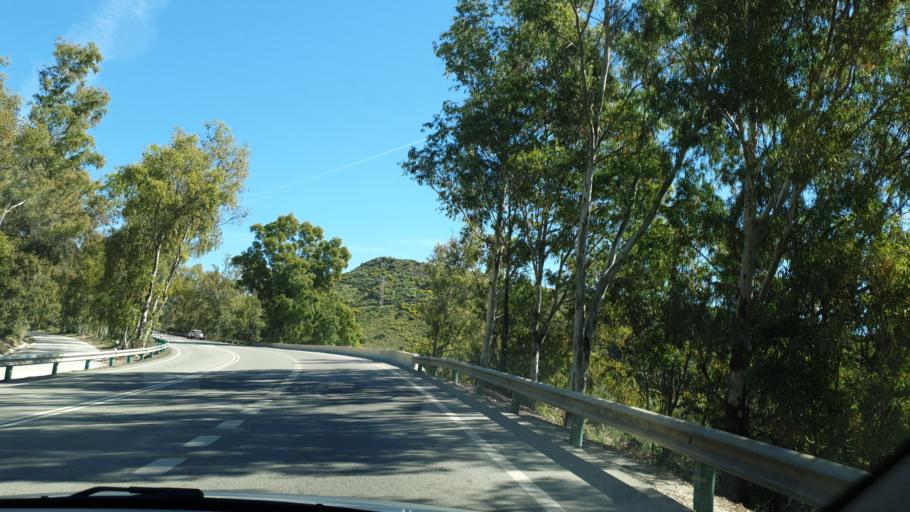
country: ES
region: Andalusia
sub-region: Provincia de Malaga
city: Marbella
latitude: 36.5337
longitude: -4.8698
